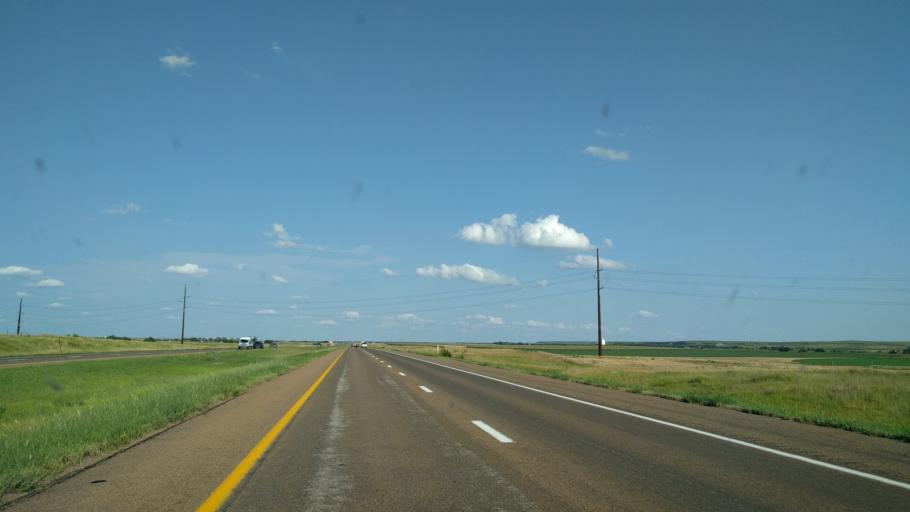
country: US
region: Kansas
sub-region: Ellis County
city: Ellis
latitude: 38.9325
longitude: -99.4624
